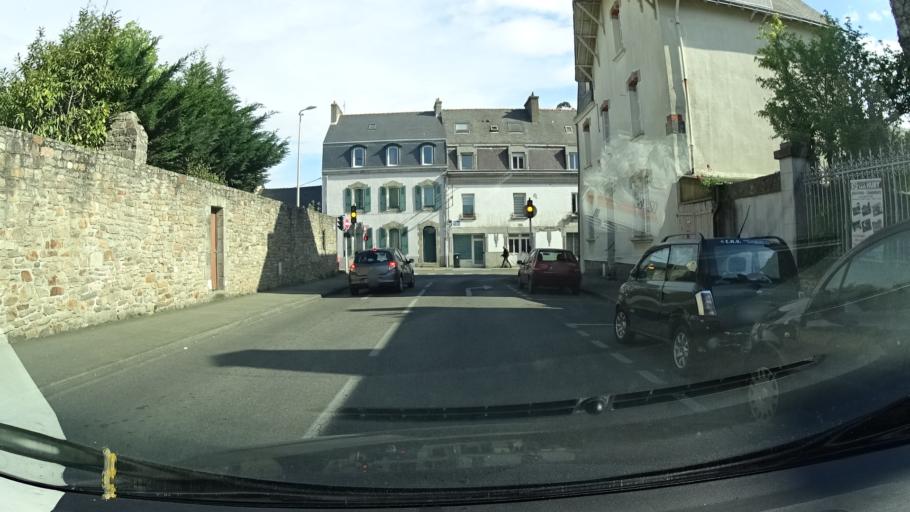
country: FR
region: Brittany
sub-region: Departement du Morbihan
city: Vannes
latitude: 47.6579
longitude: -2.7657
